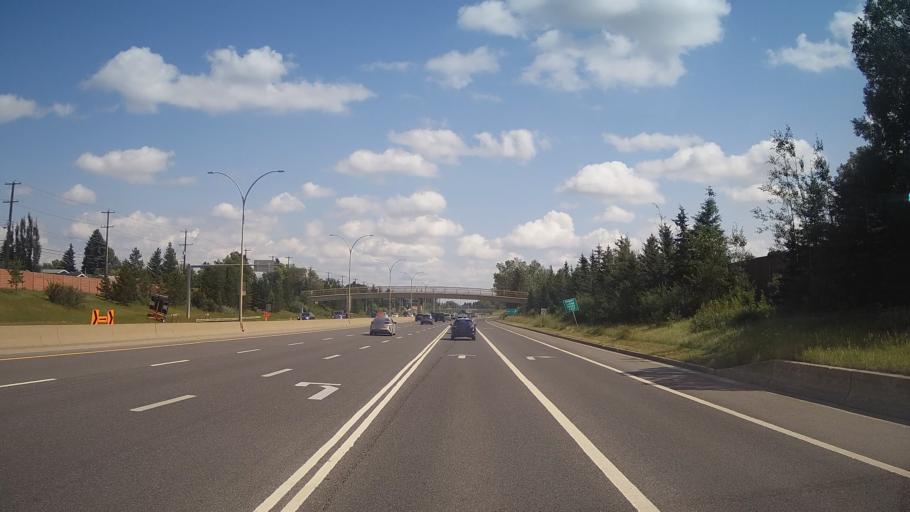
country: CA
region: Alberta
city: St. Albert
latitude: 53.5118
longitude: -113.6067
